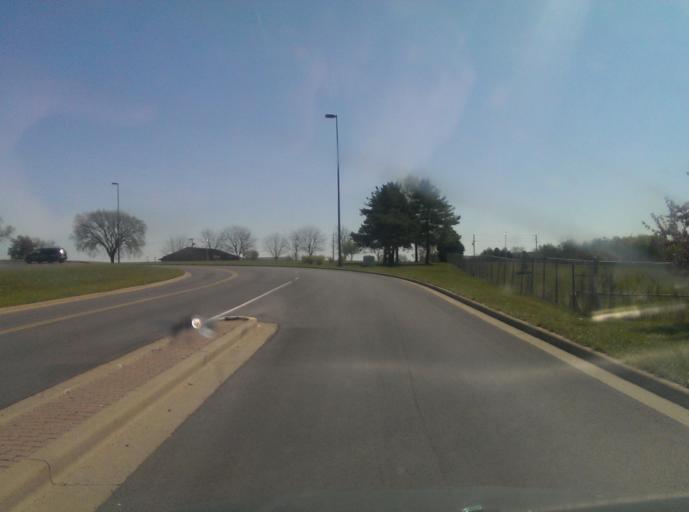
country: US
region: Kansas
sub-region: Johnson County
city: Lenexa
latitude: 38.9210
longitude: -94.7263
